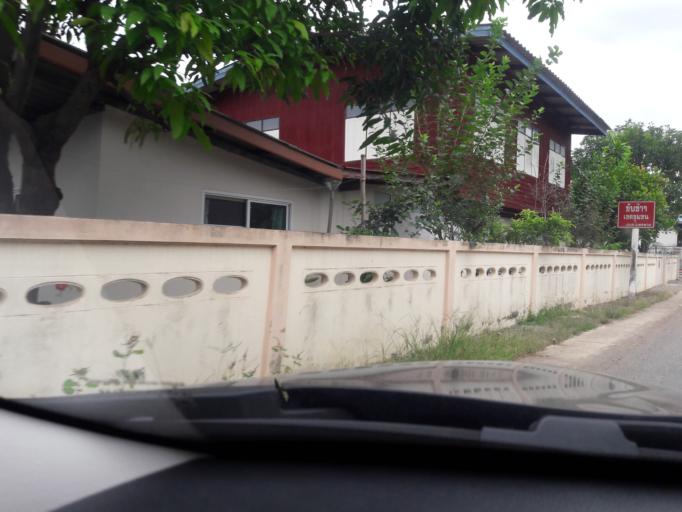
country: TH
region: Ratchaburi
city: Damnoen Saduak
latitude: 13.5909
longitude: 99.9369
